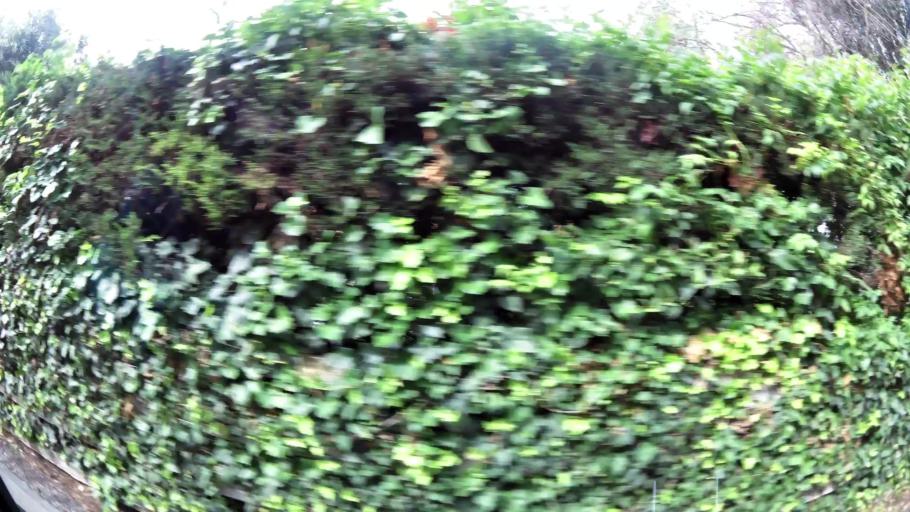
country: GR
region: Central Macedonia
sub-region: Nomos Thessalonikis
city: Panorama
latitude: 40.5893
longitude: 23.0162
